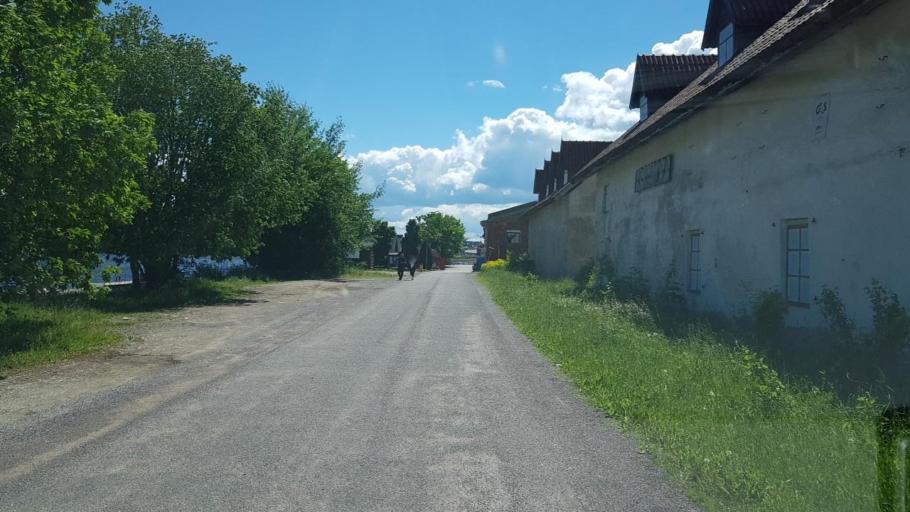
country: EE
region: Ida-Virumaa
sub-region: Narva linn
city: Narva
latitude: 59.3848
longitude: 28.2046
